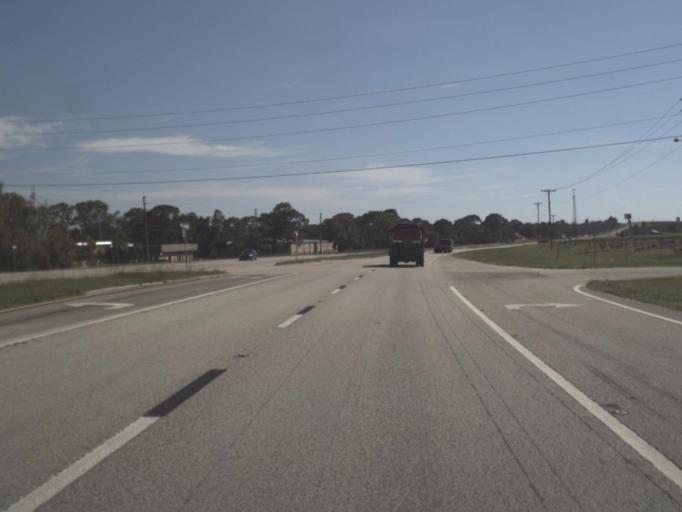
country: US
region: Florida
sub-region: Highlands County
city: Lake Placid
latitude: 27.3554
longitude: -81.3894
